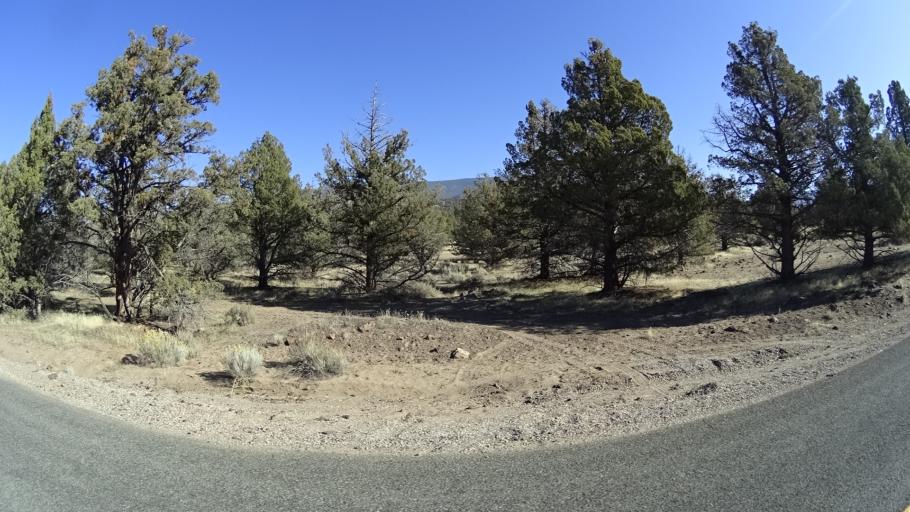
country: US
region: California
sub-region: Siskiyou County
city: Weed
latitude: 41.6071
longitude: -122.3092
